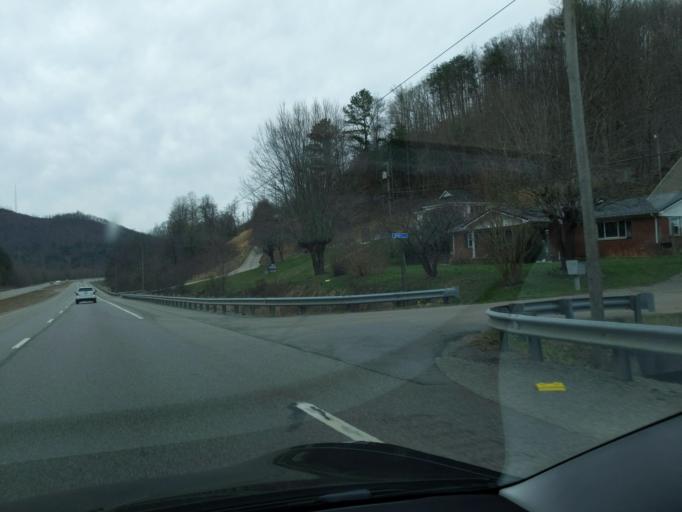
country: US
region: Kentucky
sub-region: Knox County
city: Barbourville
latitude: 36.8669
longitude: -83.8050
